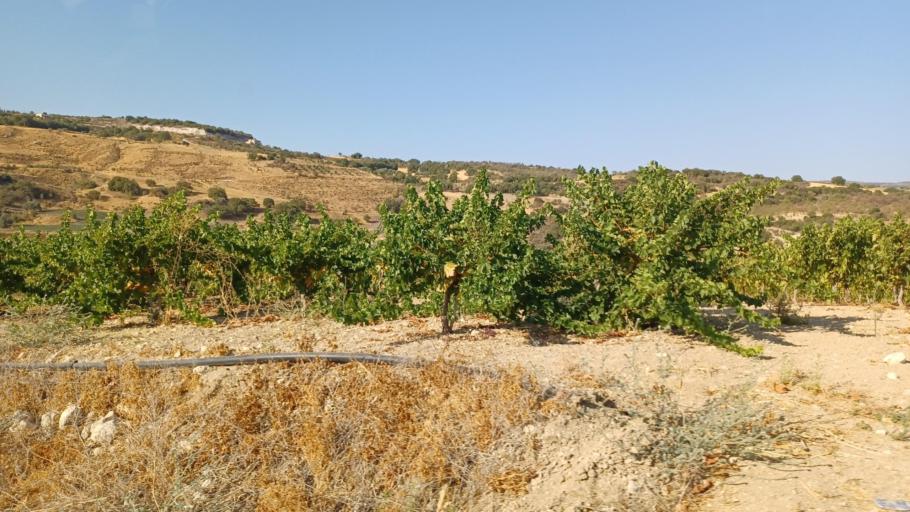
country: CY
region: Pafos
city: Polis
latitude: 34.9582
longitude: 32.4969
